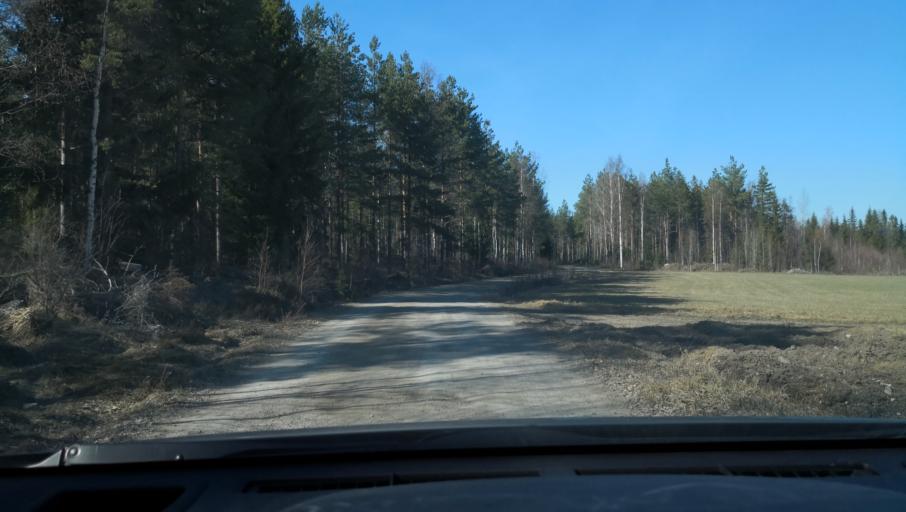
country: SE
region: Vaestmanland
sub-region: Sala Kommun
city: Sala
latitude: 59.9320
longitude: 16.4508
